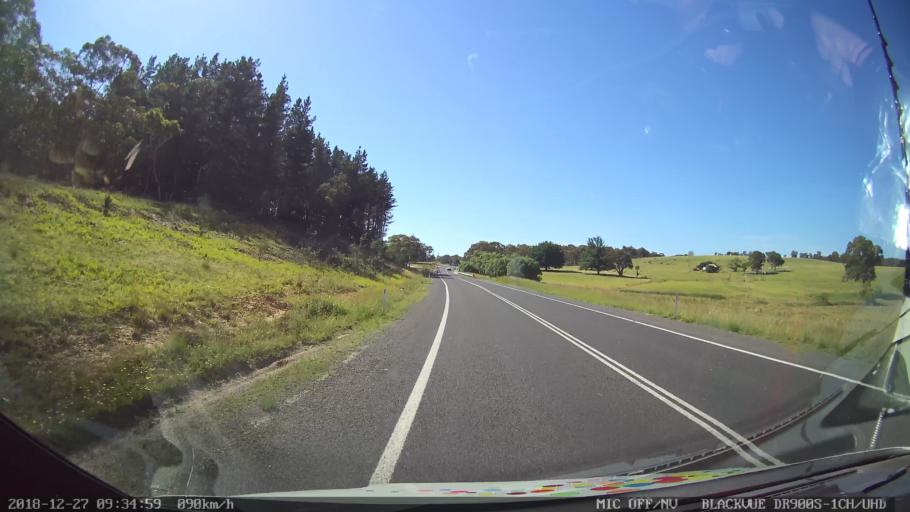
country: AU
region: New South Wales
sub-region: Lithgow
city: Portland
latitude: -33.2332
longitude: 150.0268
